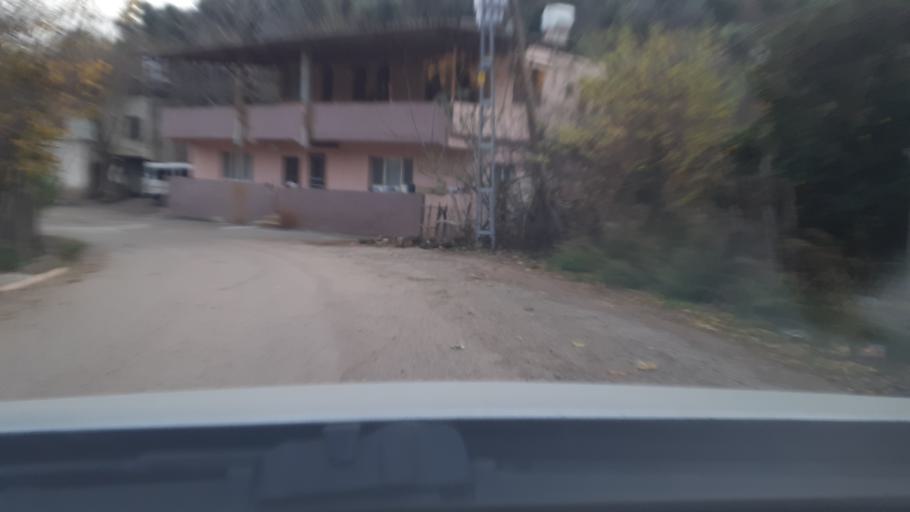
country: TR
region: Hatay
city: Kirikhan
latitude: 36.5333
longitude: 36.3145
